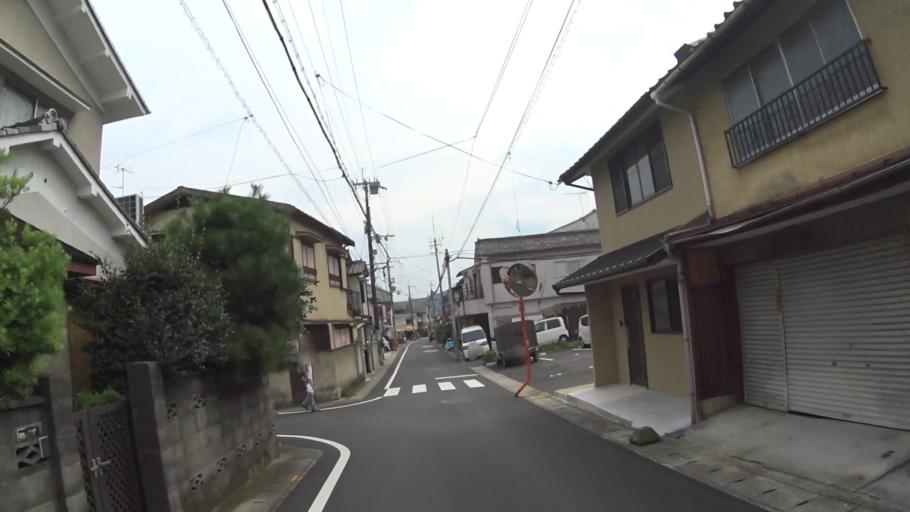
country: JP
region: Kyoto
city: Kyoto
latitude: 34.9929
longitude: 135.8004
